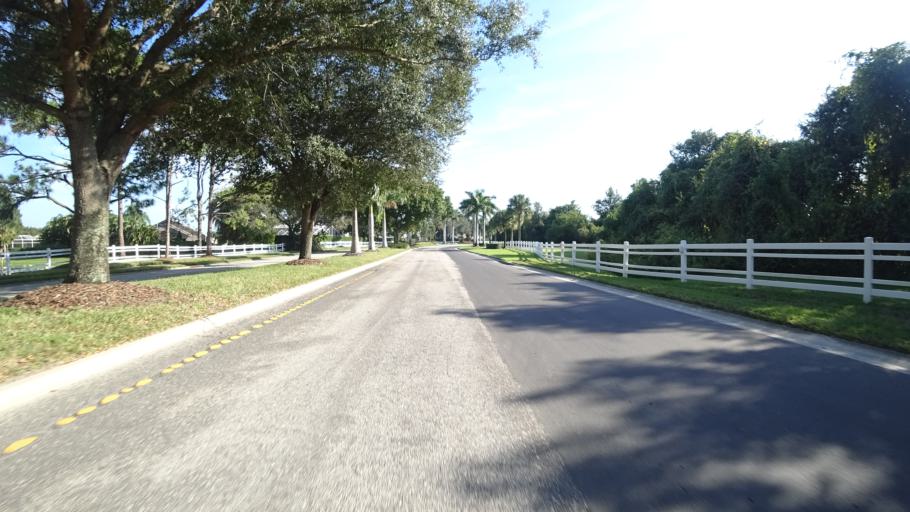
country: US
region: Florida
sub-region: Sarasota County
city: Desoto Lakes
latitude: 27.4167
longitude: -82.4842
